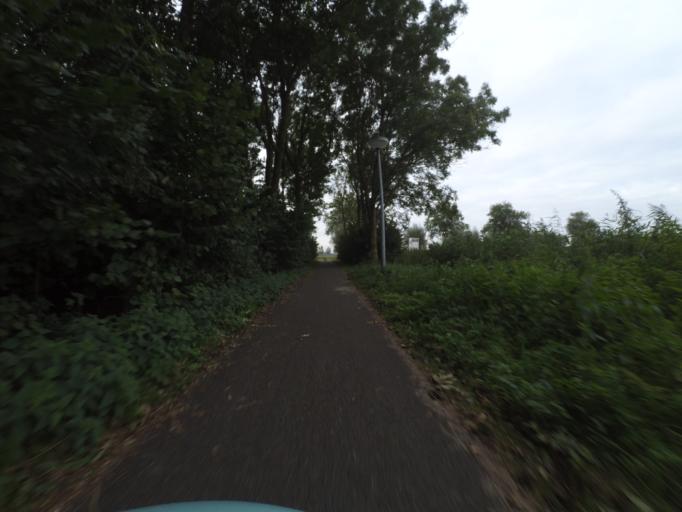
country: NL
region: Gelderland
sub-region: Gemeente Culemborg
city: Culemborg
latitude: 51.9466
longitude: 5.2772
